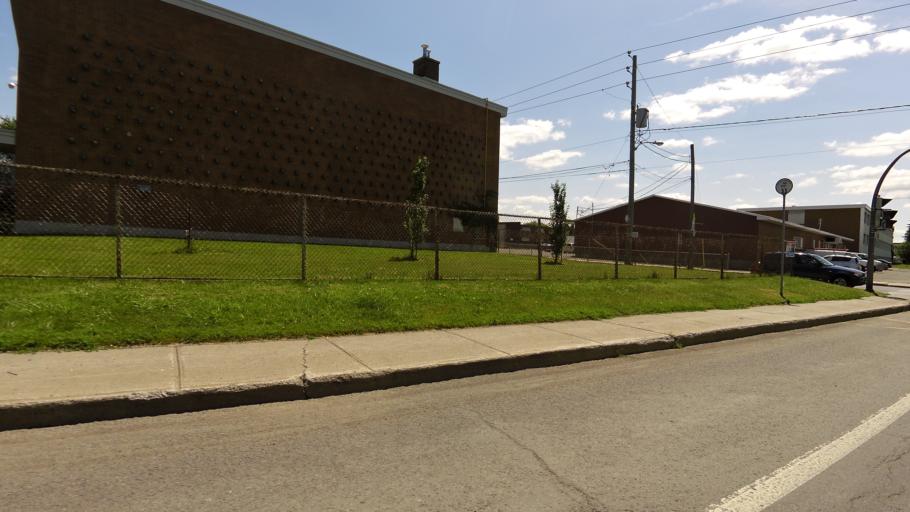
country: CA
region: Quebec
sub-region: Monteregie
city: Saint-Jean-sur-Richelieu
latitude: 45.3032
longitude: -73.2665
